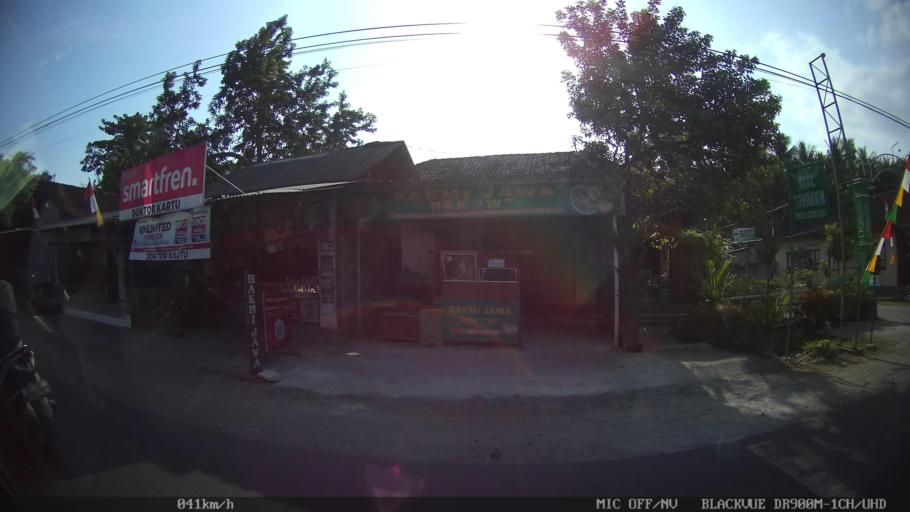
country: ID
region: Daerah Istimewa Yogyakarta
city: Bantul
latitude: -7.8887
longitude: 110.3036
